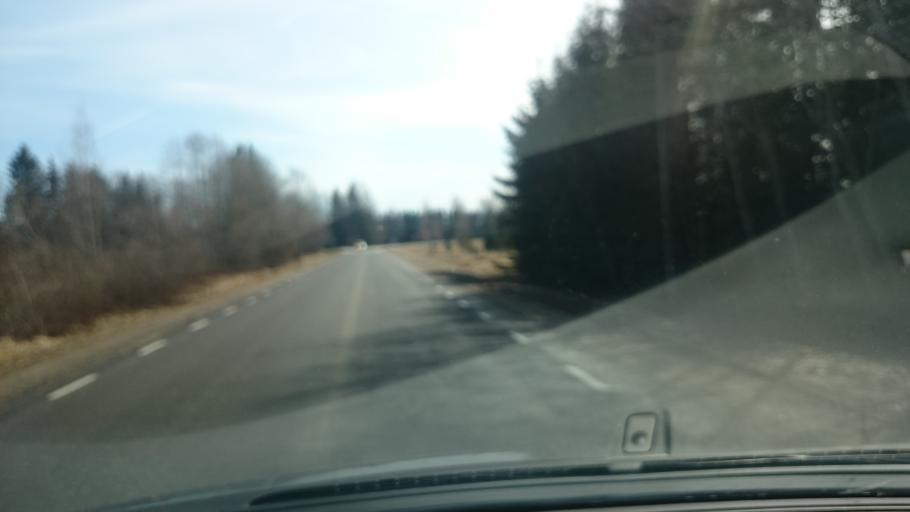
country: EE
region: Paernumaa
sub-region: Vaendra vald (alev)
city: Vandra
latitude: 58.6282
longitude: 24.9216
